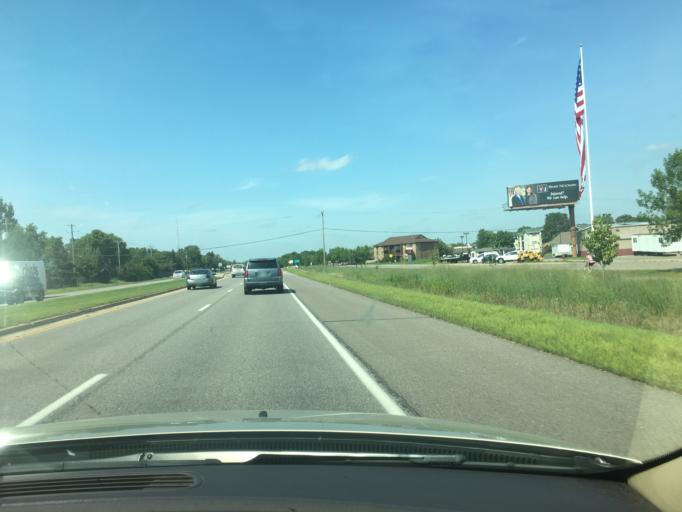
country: US
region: Minnesota
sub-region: Stearns County
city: Saint Cloud
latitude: 45.5265
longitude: -94.1626
